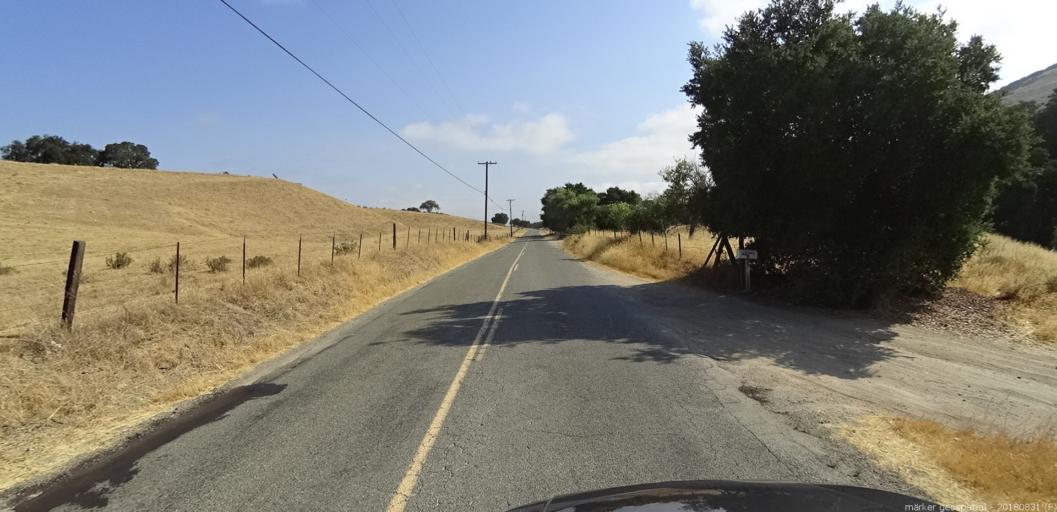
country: US
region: California
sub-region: Monterey County
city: King City
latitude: 36.1662
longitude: -121.1608
